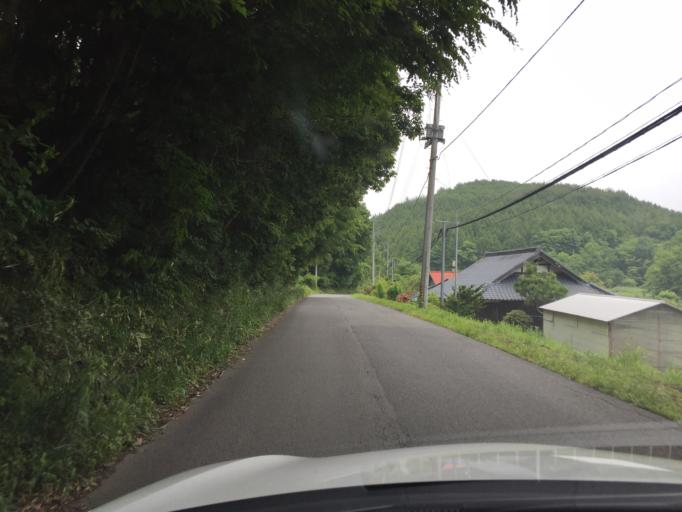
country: JP
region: Fukushima
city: Iwaki
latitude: 37.1658
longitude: 140.7076
